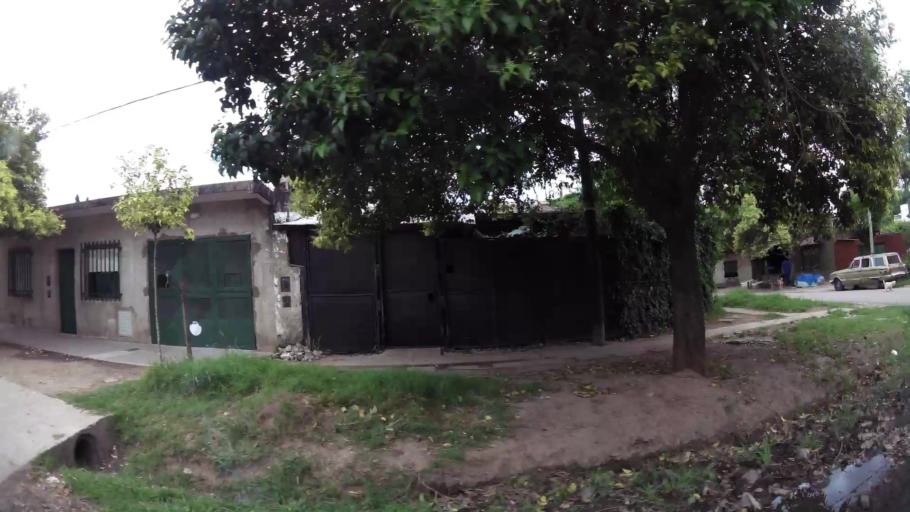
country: AR
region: Santa Fe
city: Gobernador Galvez
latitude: -32.9968
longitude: -60.6578
